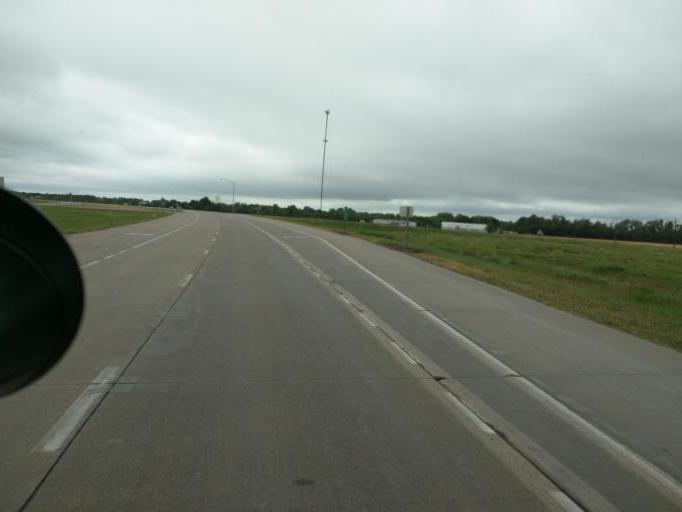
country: US
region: Kansas
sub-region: Reno County
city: South Hutchinson
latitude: 37.9753
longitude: -97.9396
